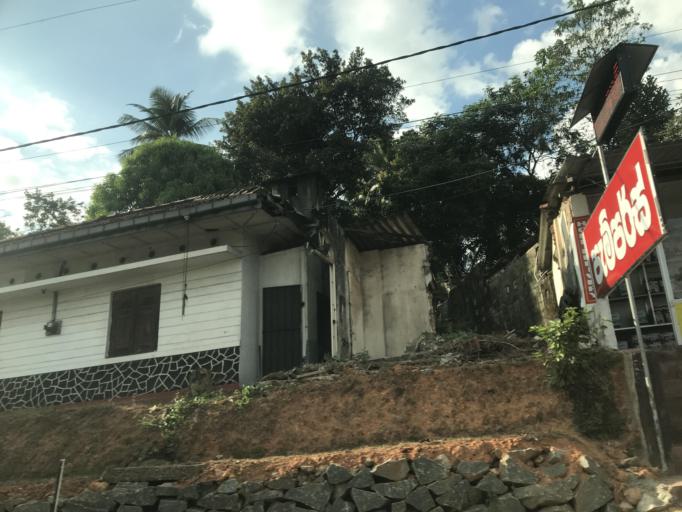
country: LK
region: Western
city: Gampaha
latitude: 7.0599
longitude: 80.0096
